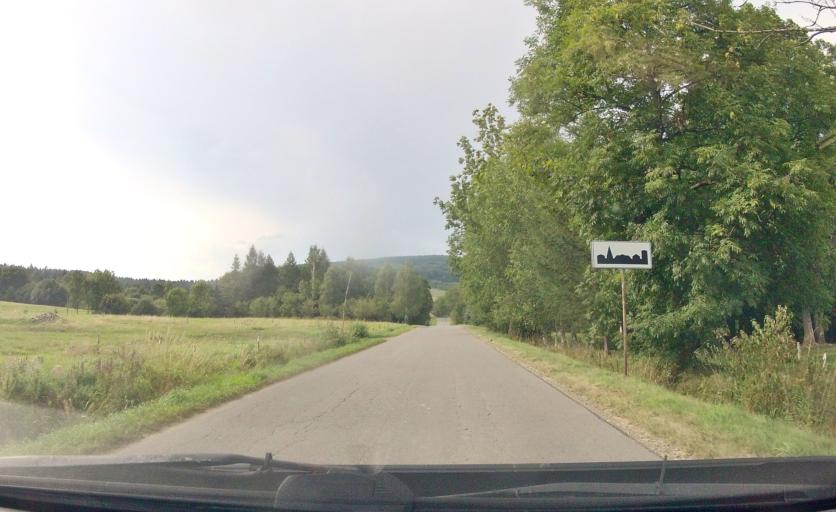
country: PL
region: Subcarpathian Voivodeship
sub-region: Powiat krosnienski
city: Dukla
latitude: 49.5166
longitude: 21.6217
